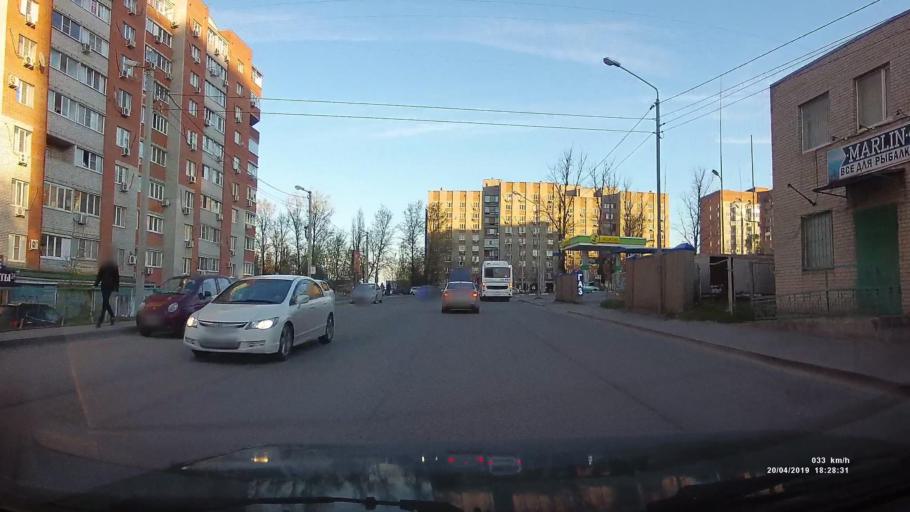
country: RU
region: Rostov
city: Aksay
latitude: 47.2419
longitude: 39.8346
